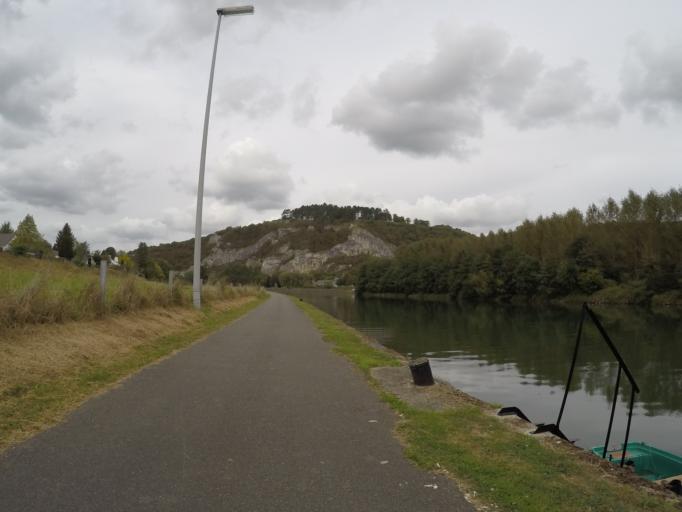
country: BE
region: Wallonia
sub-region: Province de Namur
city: Anhee
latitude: 50.2993
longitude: 4.8959
